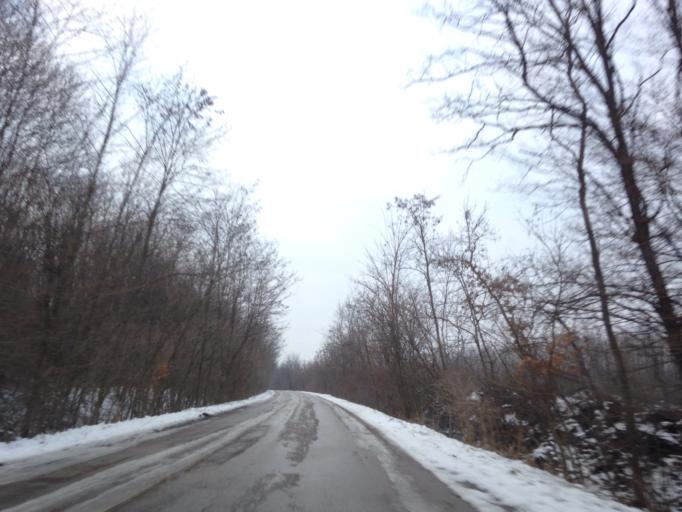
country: SK
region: Nitriansky
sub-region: Okres Nitra
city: Vrable
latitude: 48.0931
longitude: 18.3675
